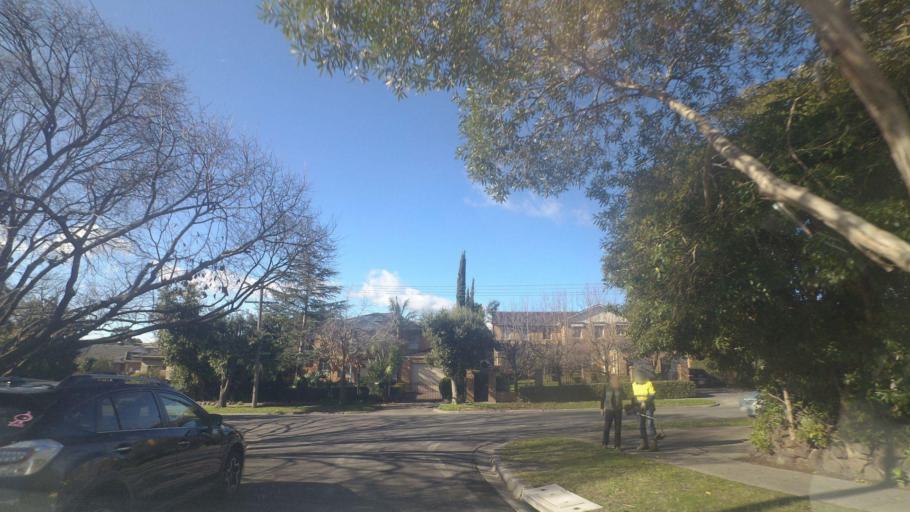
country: AU
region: Victoria
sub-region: Boroondara
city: Balwyn North
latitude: -37.7824
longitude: 145.0912
